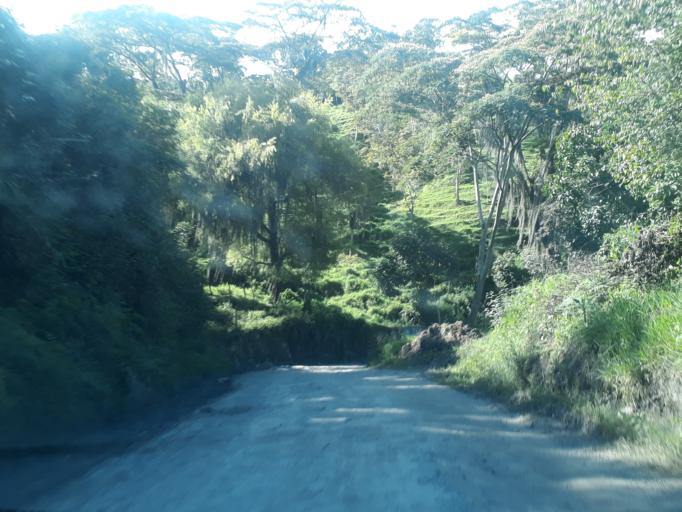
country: CO
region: Santander
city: Velez
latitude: 6.0407
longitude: -73.6536
